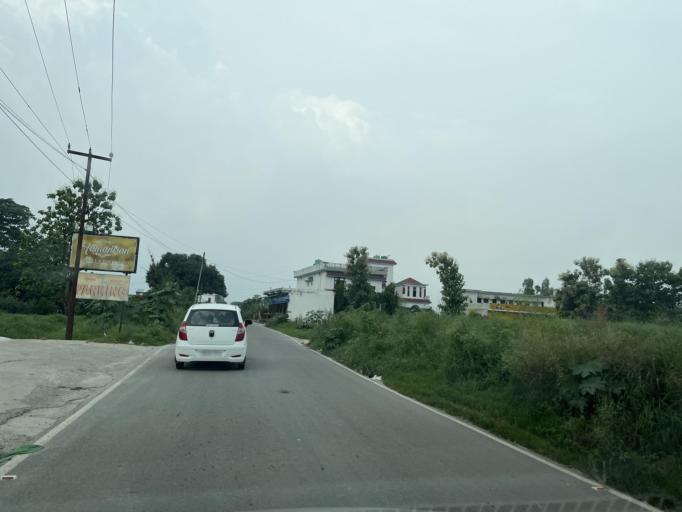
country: IN
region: Uttarakhand
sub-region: Naini Tal
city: Haldwani
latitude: 29.1867
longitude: 79.4771
